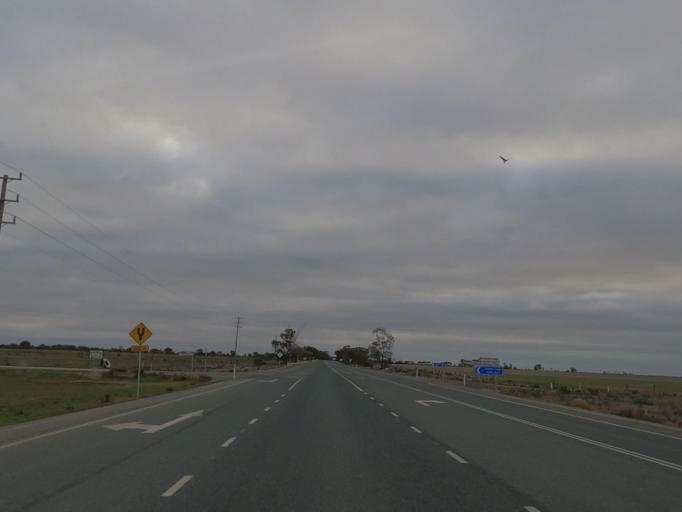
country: AU
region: Victoria
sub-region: Swan Hill
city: Swan Hill
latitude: -35.5516
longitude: 143.7703
